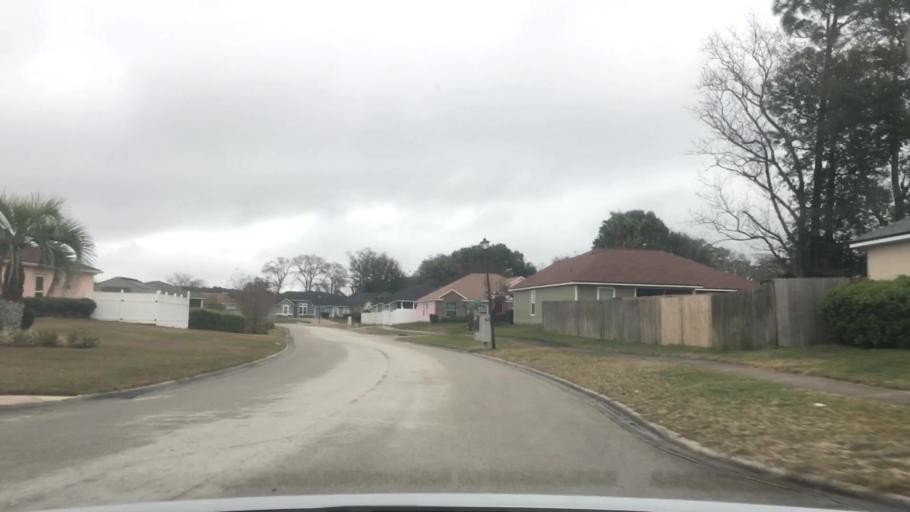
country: US
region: Florida
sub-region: Duval County
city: Jacksonville
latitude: 30.3599
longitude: -81.5757
